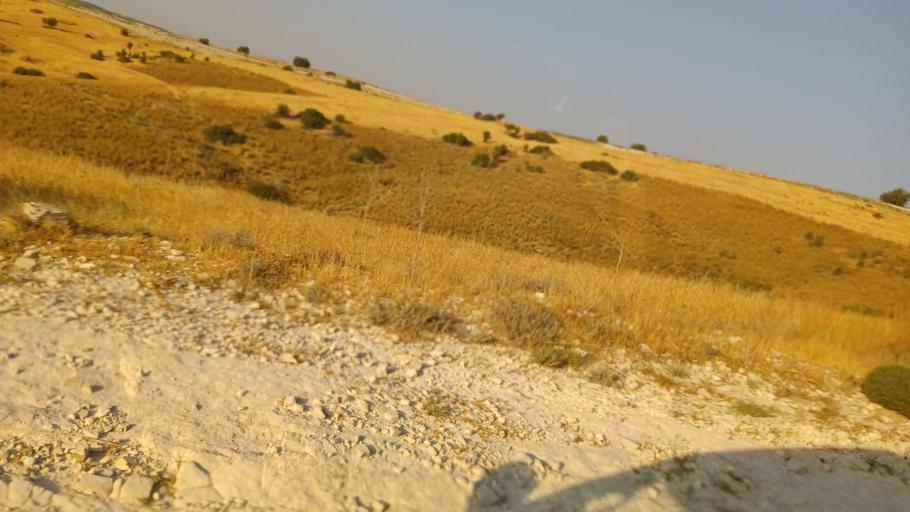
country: CY
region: Larnaka
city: Psevdas
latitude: 34.9202
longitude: 33.4844
